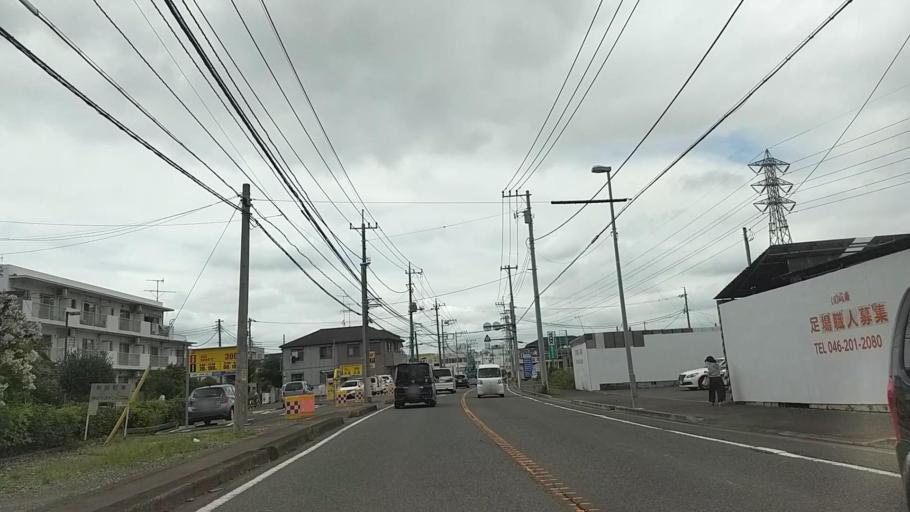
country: JP
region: Kanagawa
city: Minami-rinkan
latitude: 35.4281
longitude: 139.4679
